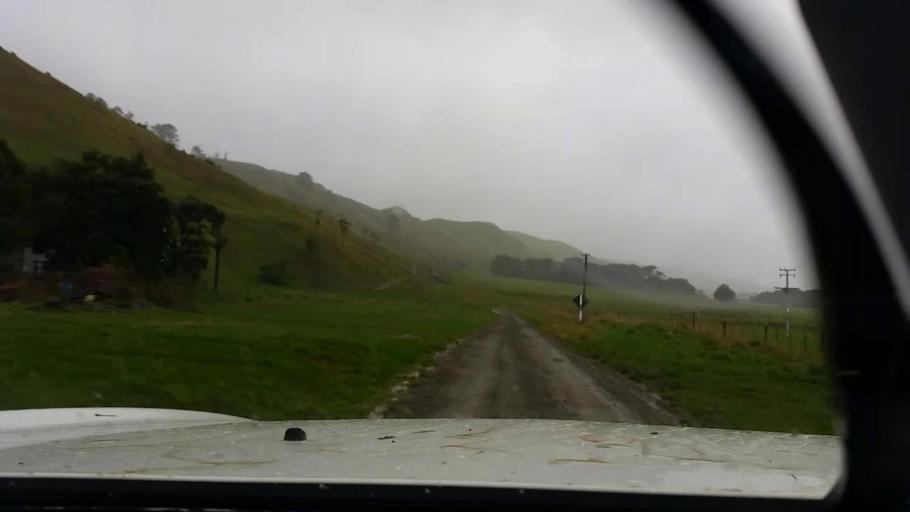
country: NZ
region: Wellington
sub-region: Masterton District
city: Masterton
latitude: -41.2609
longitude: 175.8966
